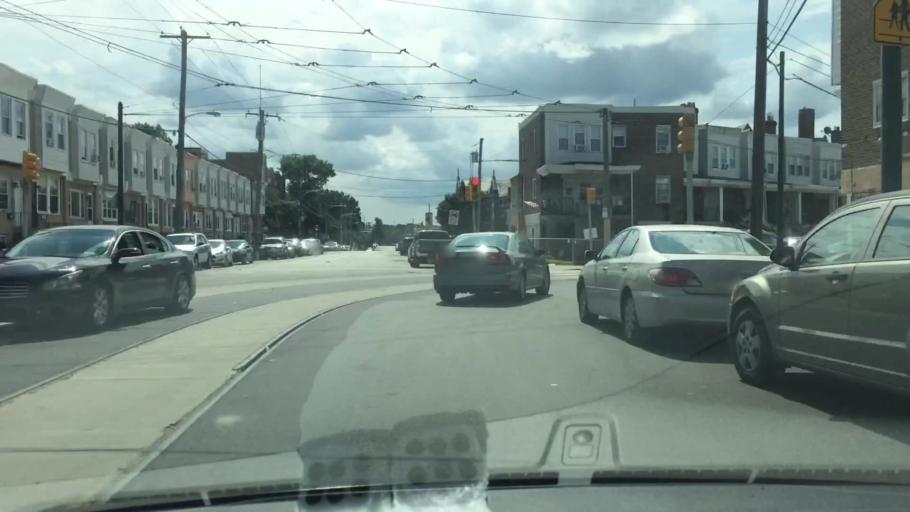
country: US
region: Pennsylvania
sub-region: Delaware County
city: Yeadon
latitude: 39.9288
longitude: -75.2385
